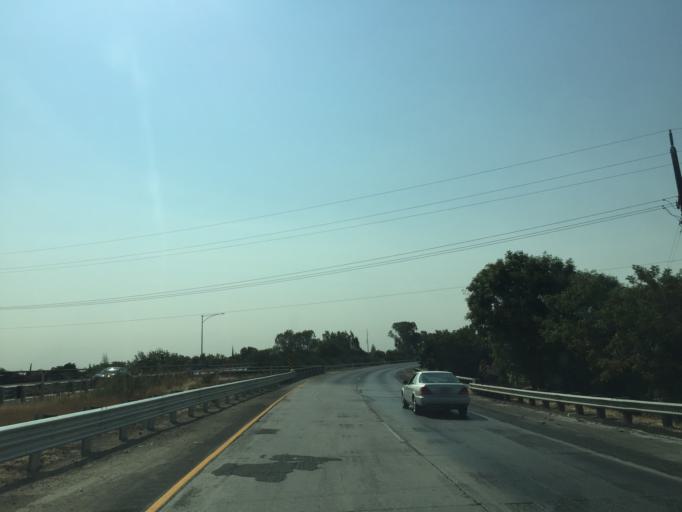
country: US
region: California
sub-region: Merced County
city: Merced
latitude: 37.2953
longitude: -120.4769
